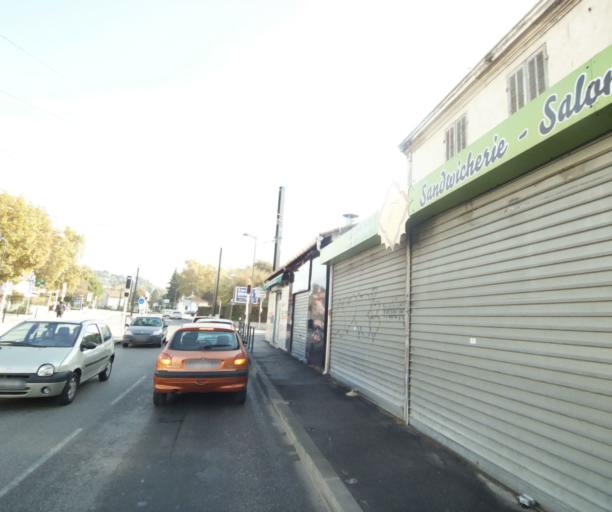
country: FR
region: Provence-Alpes-Cote d'Azur
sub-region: Departement des Bouches-du-Rhone
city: Aubagne
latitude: 43.2852
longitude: 5.5536
